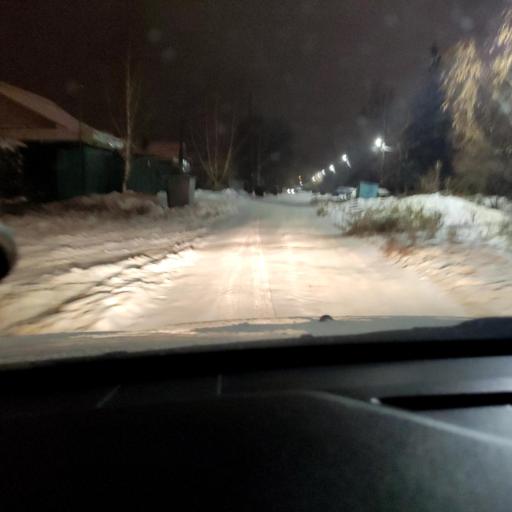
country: RU
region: Samara
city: Smyshlyayevka
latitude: 53.2423
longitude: 50.3226
